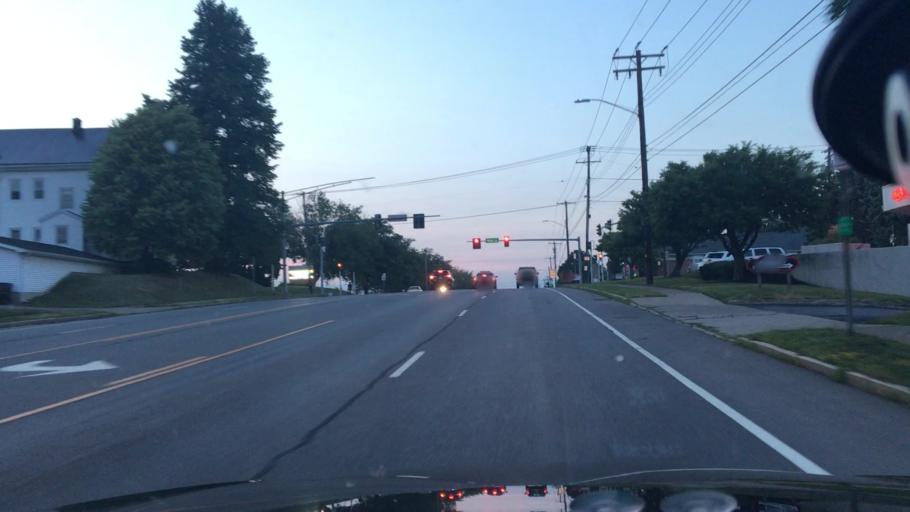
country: US
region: New York
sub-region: Erie County
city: West Seneca
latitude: 42.8327
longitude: -78.7537
